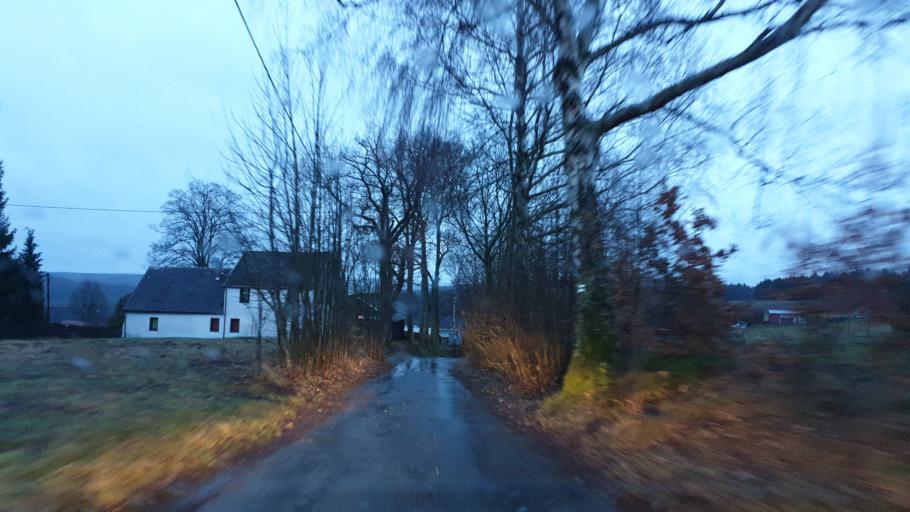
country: DE
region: Saxony
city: Bad Elster
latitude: 50.3104
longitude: 12.2281
